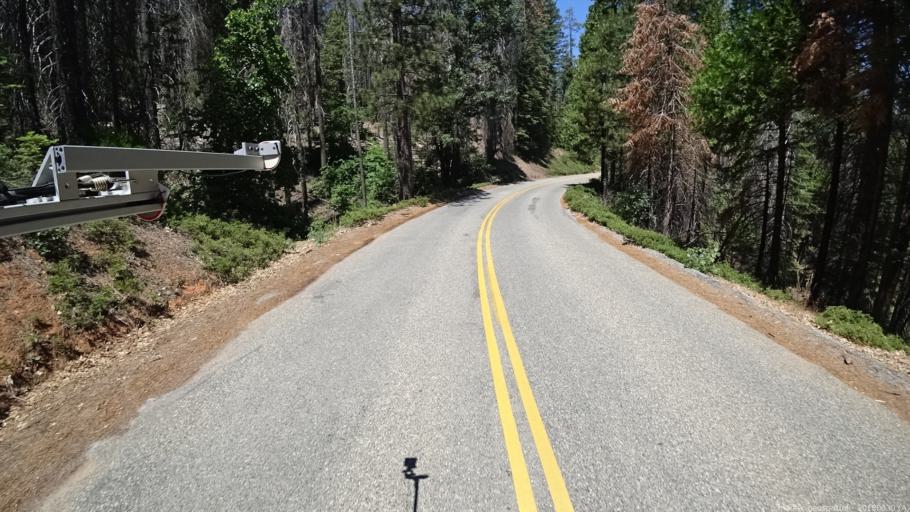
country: US
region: California
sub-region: Madera County
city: Oakhurst
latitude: 37.3429
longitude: -119.3808
